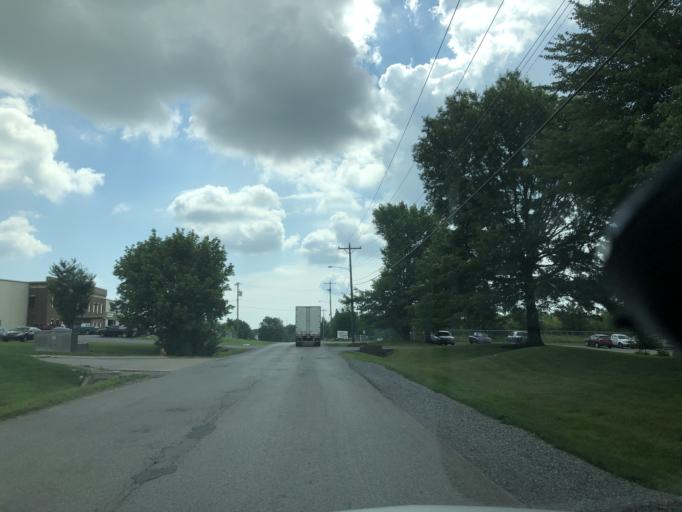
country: US
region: Tennessee
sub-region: Rutherford County
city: La Vergne
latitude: 36.0120
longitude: -86.6068
